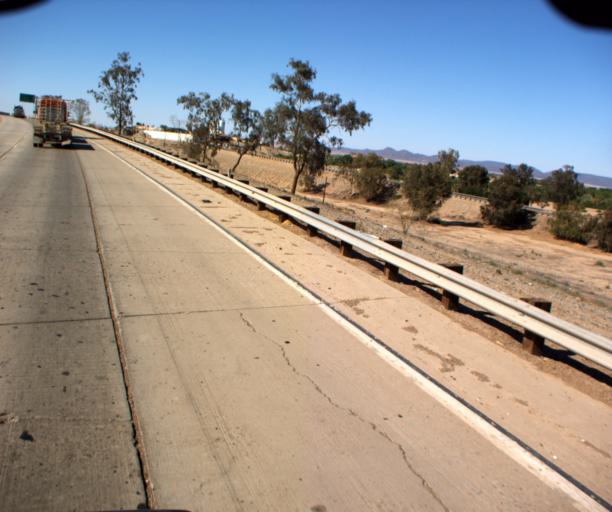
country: US
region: Arizona
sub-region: Yuma County
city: Yuma
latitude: 32.7226
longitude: -114.6135
